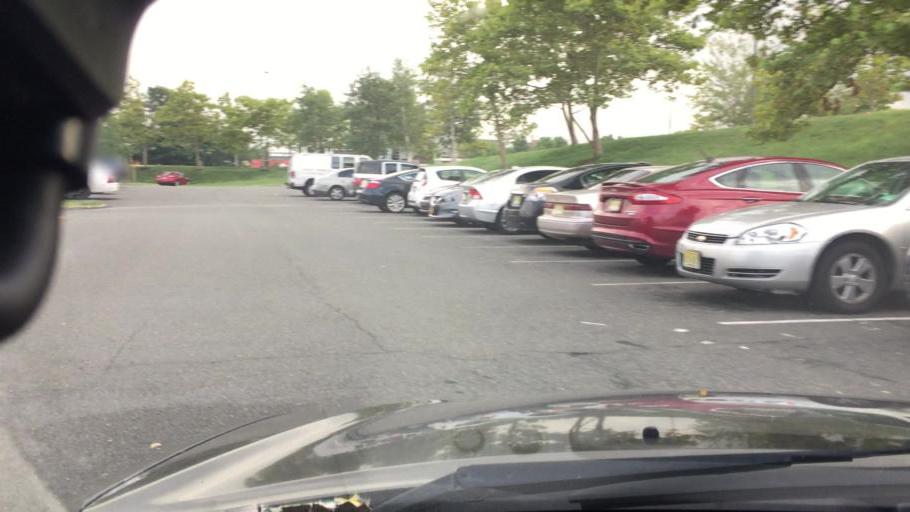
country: US
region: New Jersey
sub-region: Union County
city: Elizabeth
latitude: 40.6575
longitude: -74.1701
